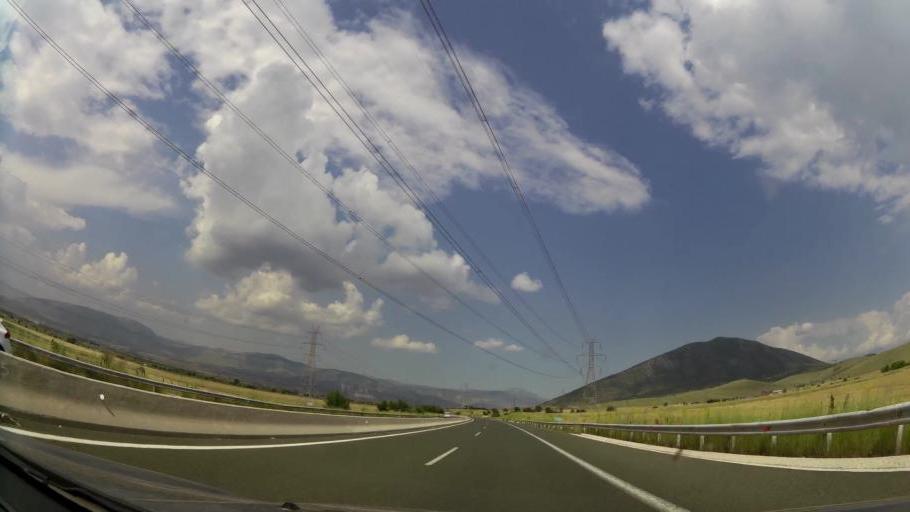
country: GR
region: West Macedonia
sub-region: Nomos Kozanis
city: Koila
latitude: 40.3589
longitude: 21.8439
